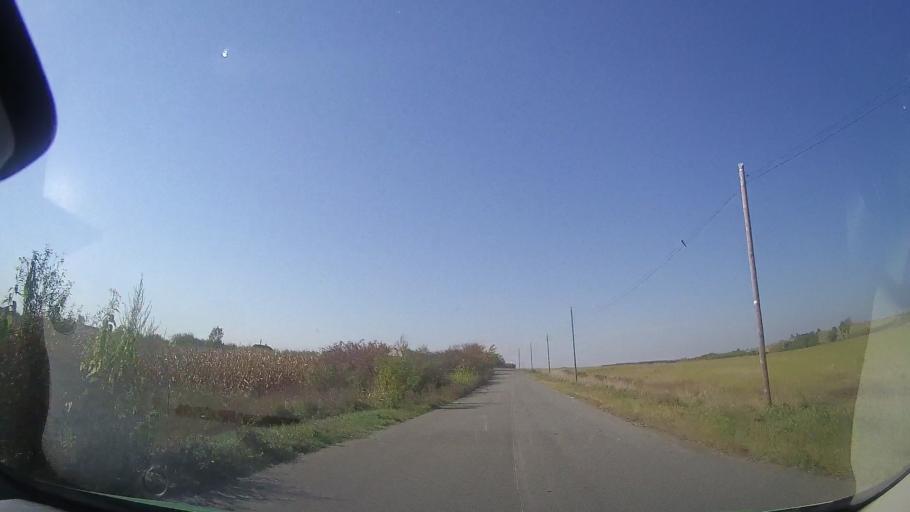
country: RO
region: Timis
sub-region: Comuna Ghizela
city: Ghizela
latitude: 45.8284
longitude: 21.7511
